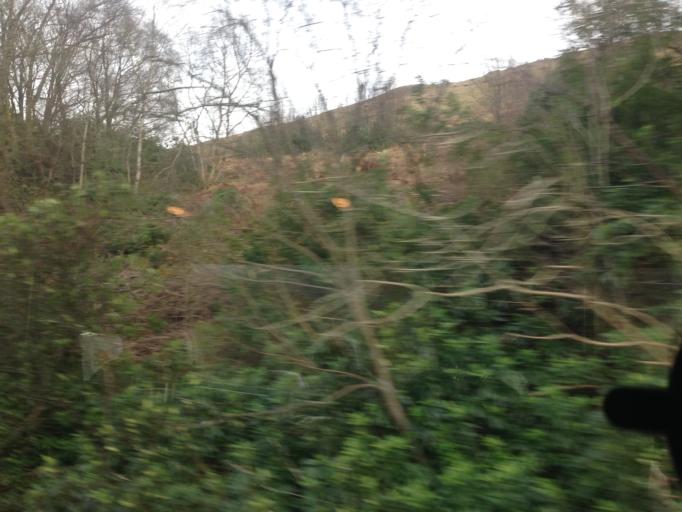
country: GB
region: Scotland
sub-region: Argyll and Bute
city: Garelochhead
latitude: 56.1947
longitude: -4.7415
